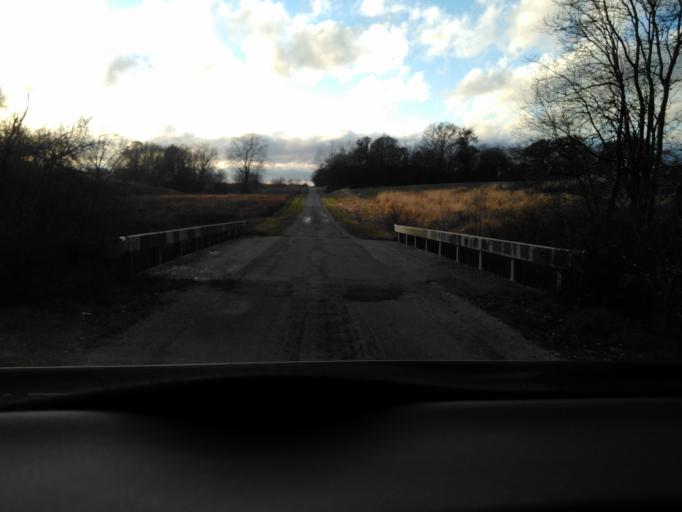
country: US
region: Illinois
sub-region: Effingham County
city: Altamont
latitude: 38.9512
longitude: -88.6945
